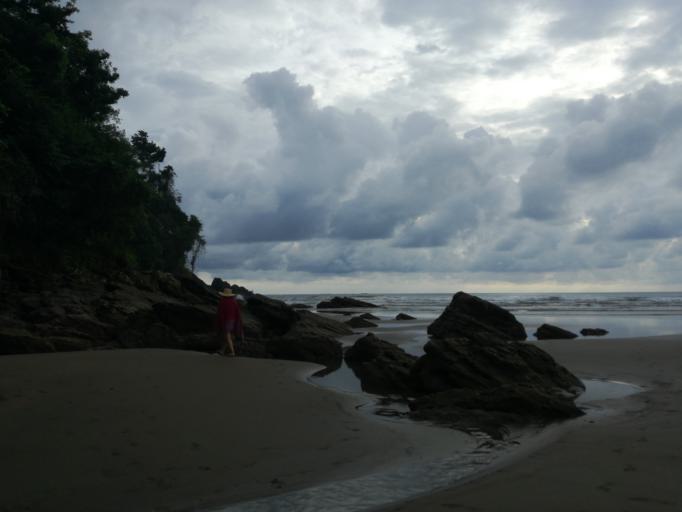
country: CR
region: San Jose
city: Mercedes
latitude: 9.1446
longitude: -83.7278
